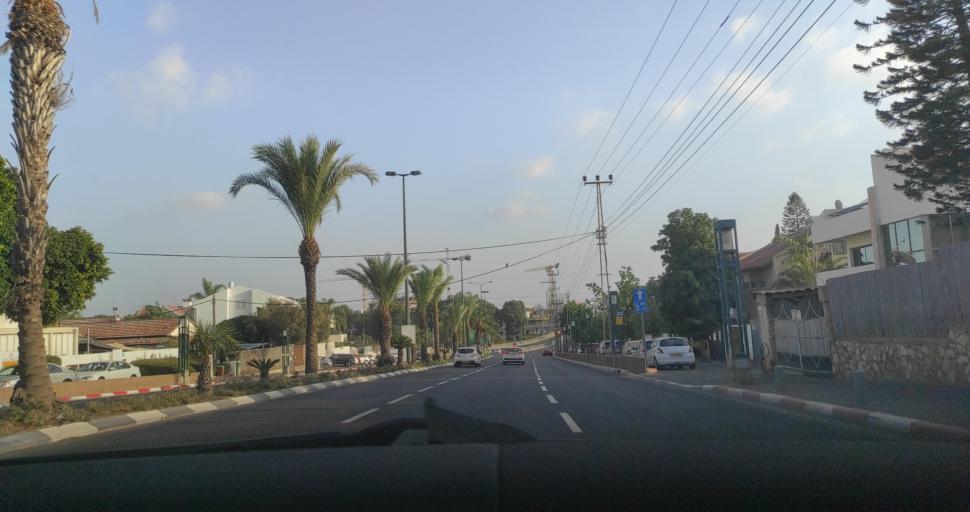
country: IL
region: Tel Aviv
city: Bene Beraq
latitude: 32.1089
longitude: 34.8265
